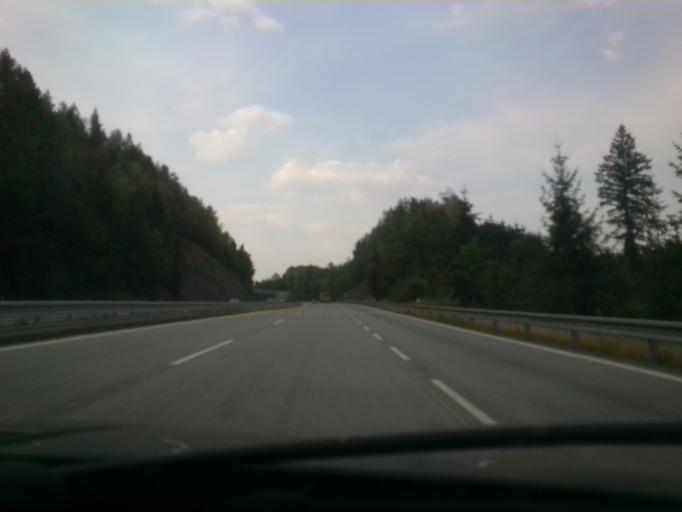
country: CZ
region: Central Bohemia
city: Divisov
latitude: 49.7909
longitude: 14.9256
